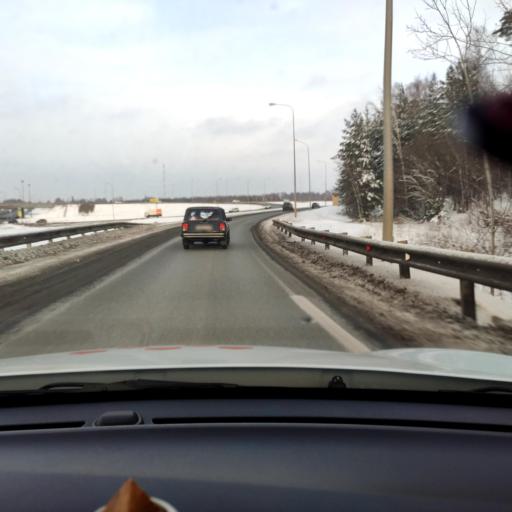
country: RU
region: Tatarstan
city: Osinovo
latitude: 55.8550
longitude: 48.8549
